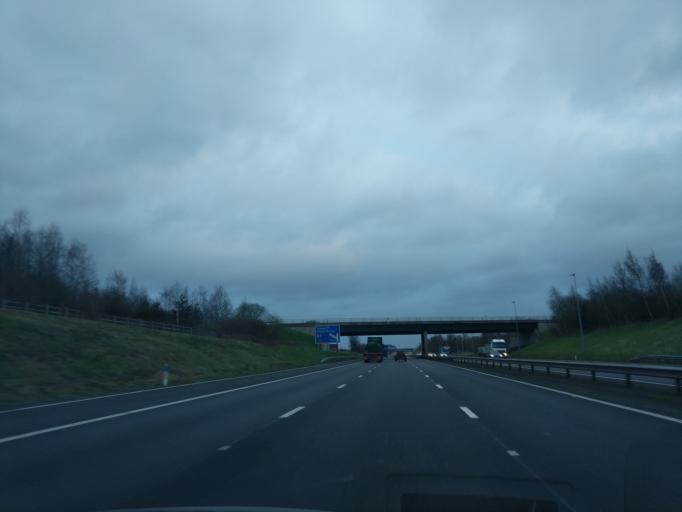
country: GB
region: England
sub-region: Staffordshire
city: Shenstone
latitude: 52.6482
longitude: -1.8358
